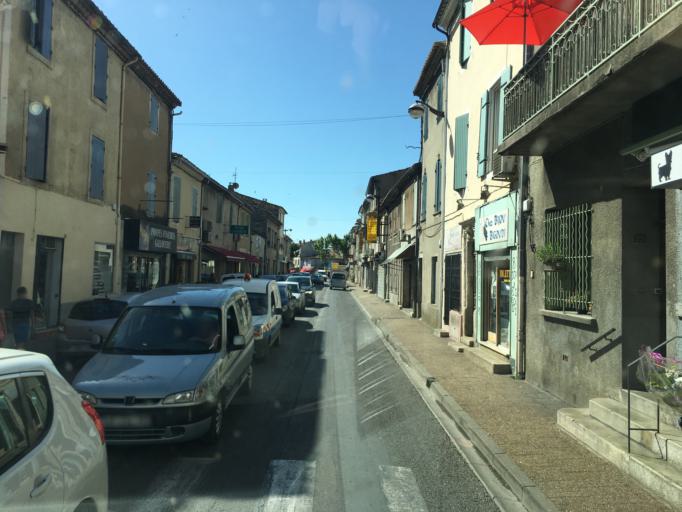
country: FR
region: Languedoc-Roussillon
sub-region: Departement du Gard
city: Saint-Gilles
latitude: 43.6751
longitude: 4.4314
